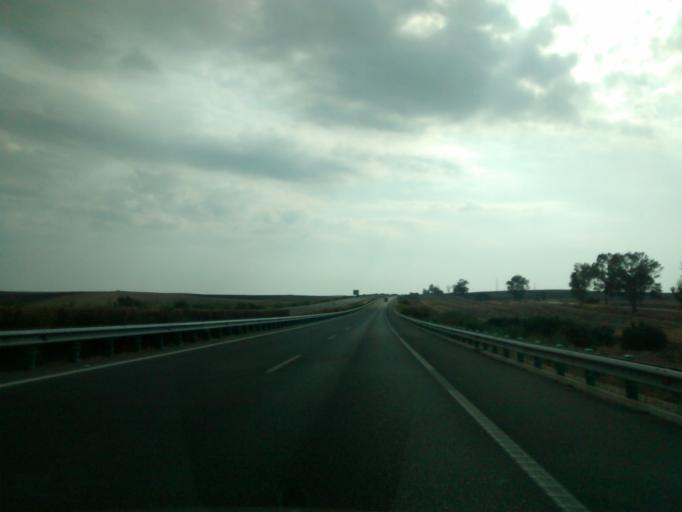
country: ES
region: Andalusia
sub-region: Provincia de Cadiz
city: Arcos de la Frontera
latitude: 36.7369
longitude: -5.8909
